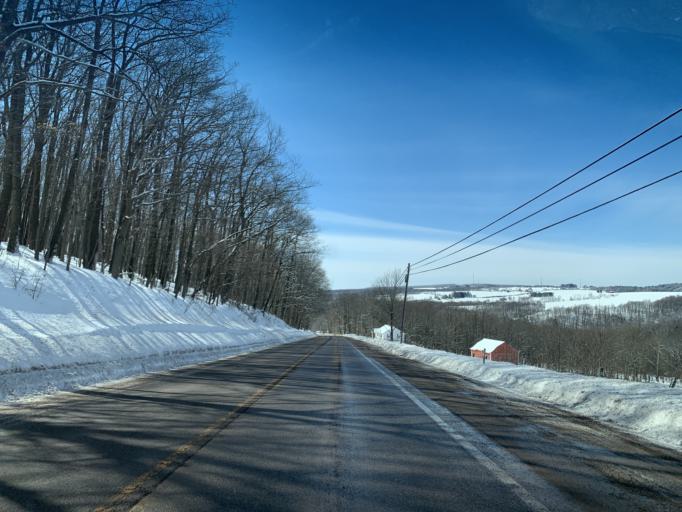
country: US
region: Pennsylvania
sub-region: Somerset County
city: Meyersdale
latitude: 39.7042
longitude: -79.2186
